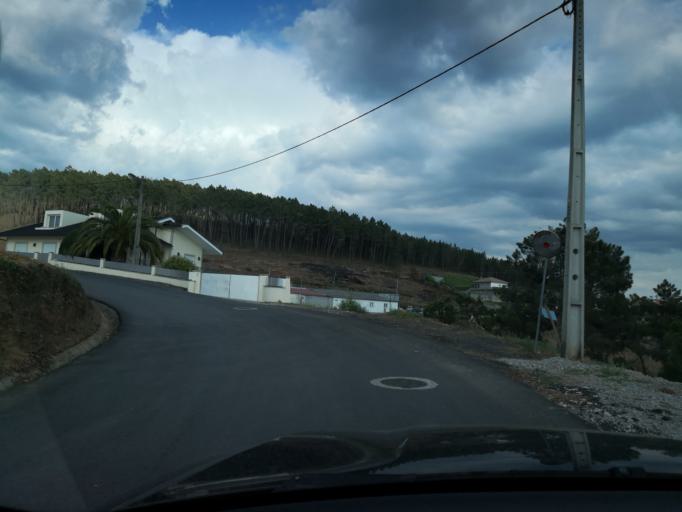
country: PT
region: Vila Real
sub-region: Sabrosa
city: Vilela
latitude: 41.2206
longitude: -7.6760
